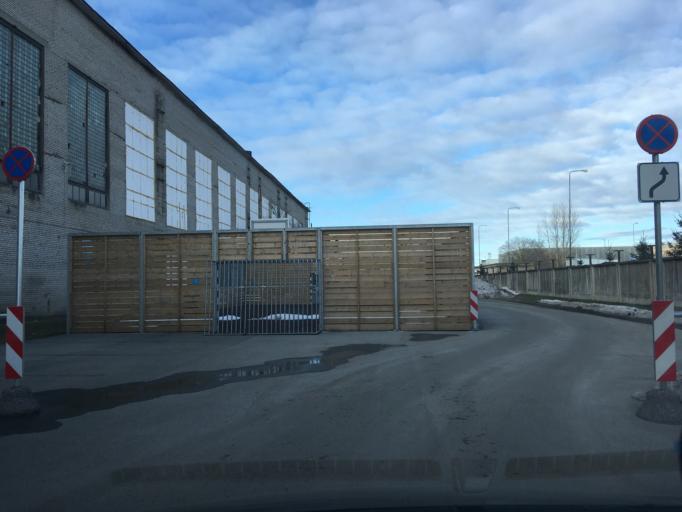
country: EE
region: Harju
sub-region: Tallinna linn
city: Tallinn
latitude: 59.4191
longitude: 24.8090
